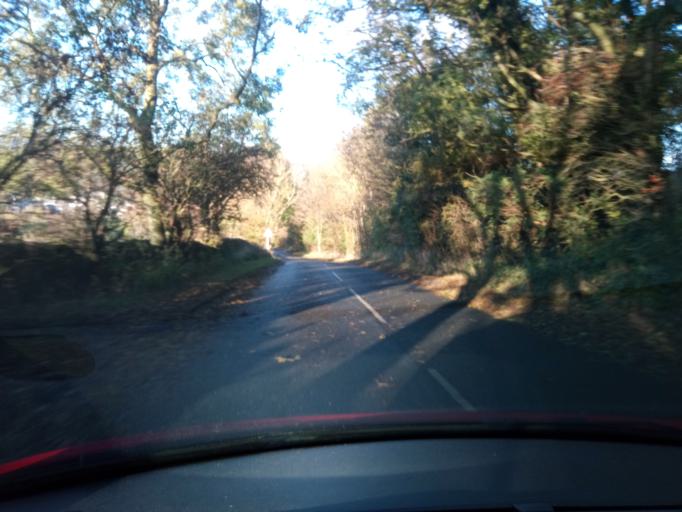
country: GB
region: England
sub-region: County Durham
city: Wolsingham
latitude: 54.7234
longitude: -1.8879
